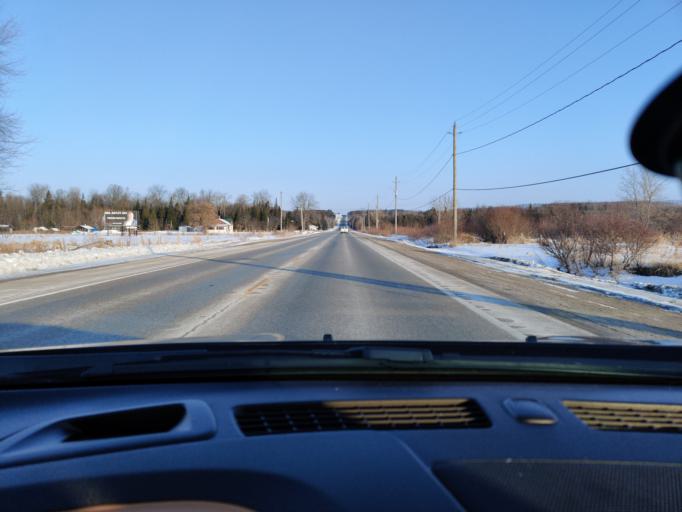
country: CA
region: Ontario
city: Barrie
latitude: 44.3582
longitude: -79.7678
